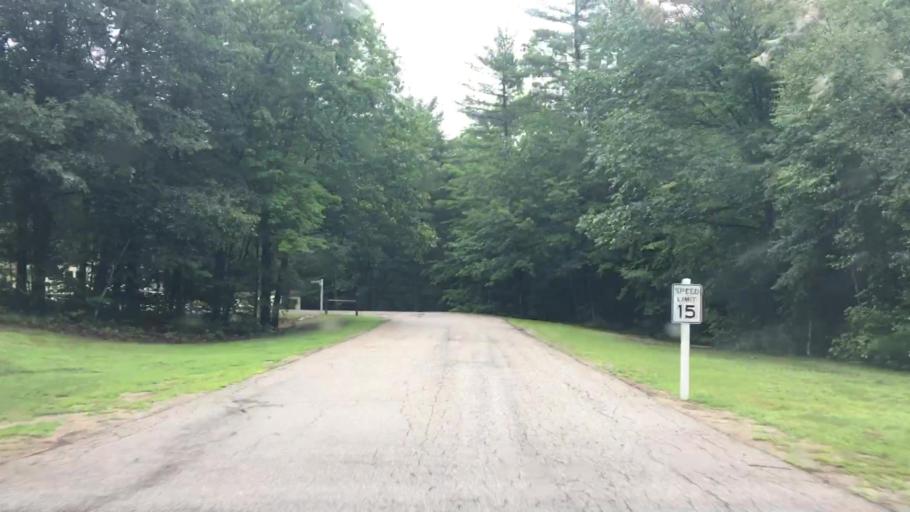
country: US
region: New Hampshire
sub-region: Carroll County
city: Conway
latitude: 43.9925
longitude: -71.0982
